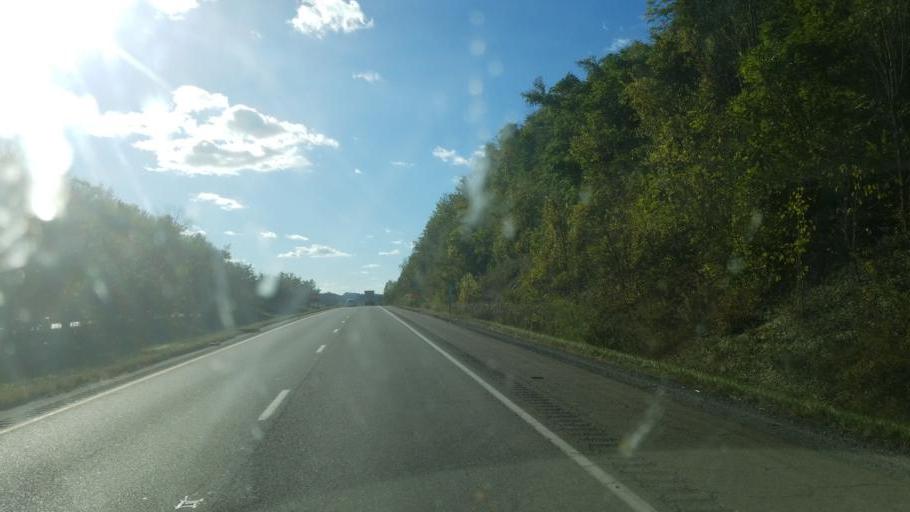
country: US
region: Ohio
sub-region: Belmont County
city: Bethesda
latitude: 40.0595
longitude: -81.1299
